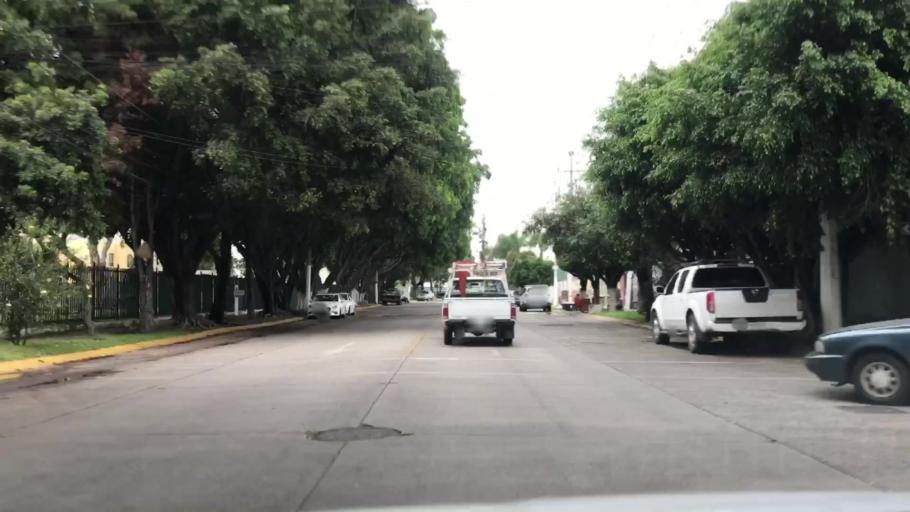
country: MX
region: Jalisco
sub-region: Tlajomulco de Zuniga
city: Palomar
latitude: 20.6387
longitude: -103.4377
